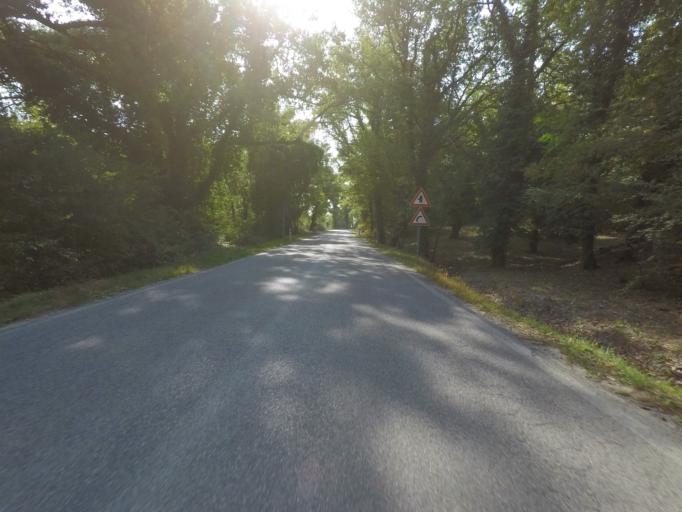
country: IT
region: Tuscany
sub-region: Provincia di Siena
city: Belverde
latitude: 43.4113
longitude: 11.3521
